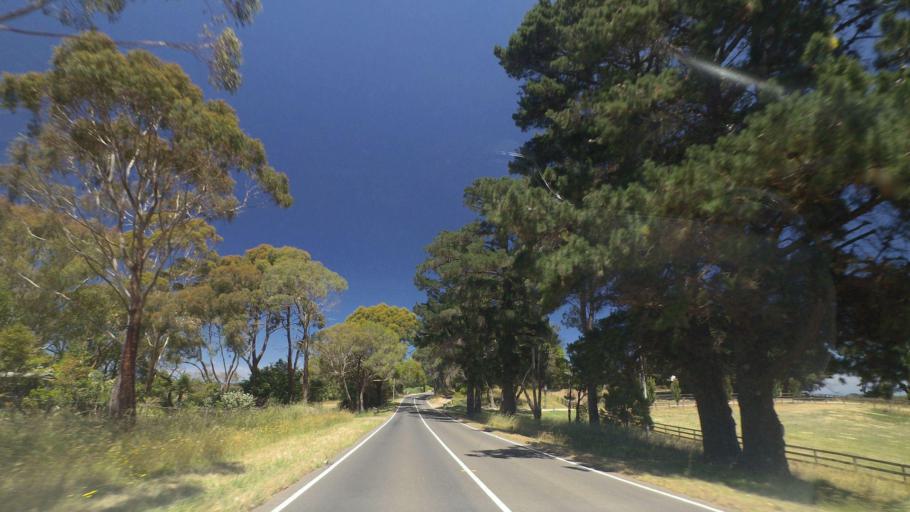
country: AU
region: Victoria
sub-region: Mornington Peninsula
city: Dromana
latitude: -38.3755
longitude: 144.9767
